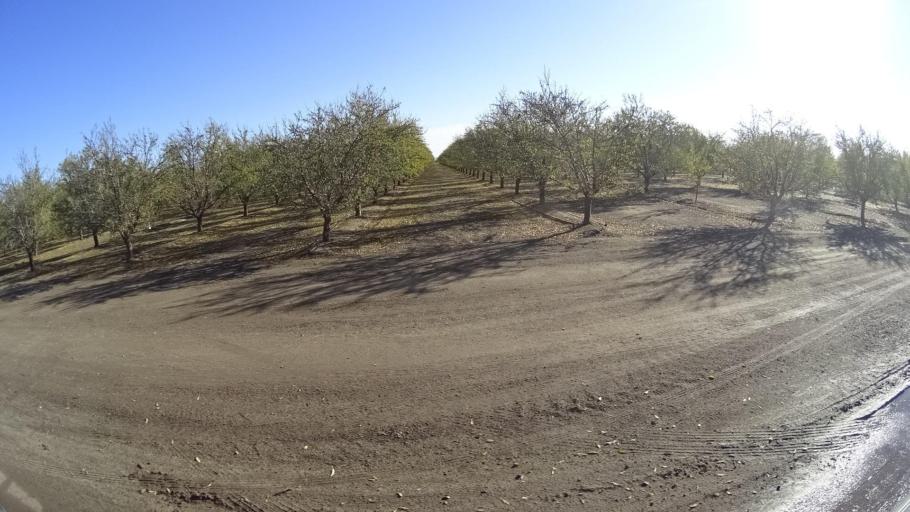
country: US
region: California
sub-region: Kern County
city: Delano
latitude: 35.7184
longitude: -119.3119
